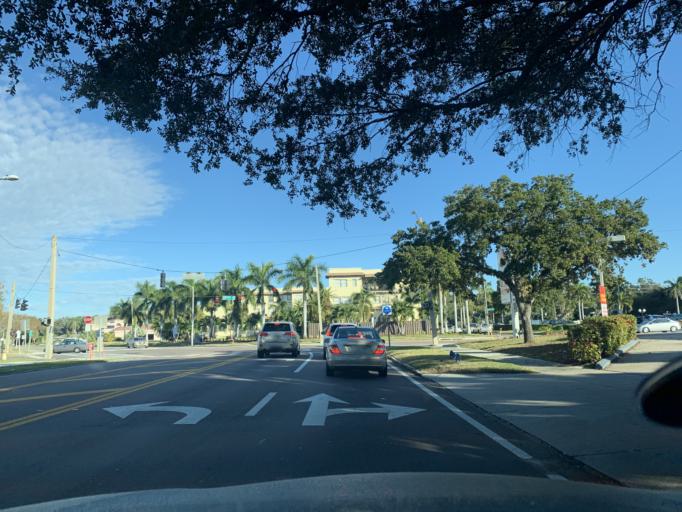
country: US
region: Florida
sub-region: Pinellas County
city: South Pasadena
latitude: 27.7704
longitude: -82.7409
